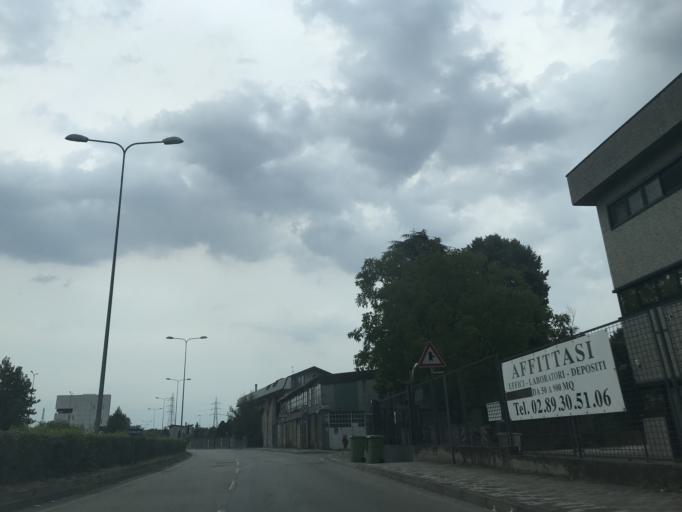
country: IT
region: Lombardy
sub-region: Citta metropolitana di Milano
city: Rozzano
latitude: 45.4063
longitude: 9.1558
